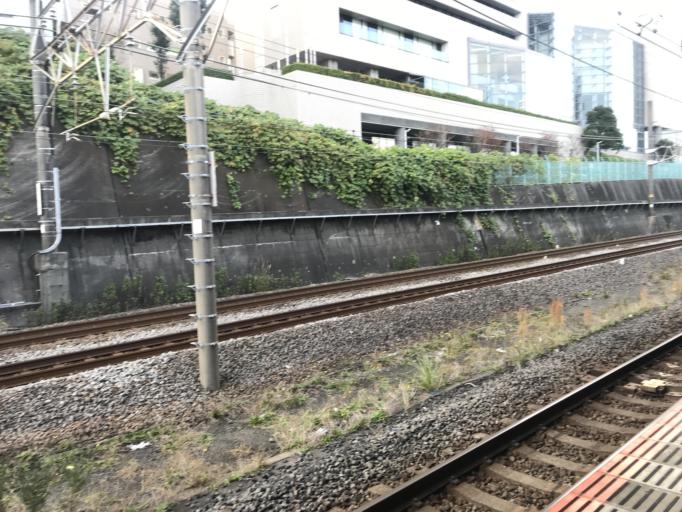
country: JP
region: Kanagawa
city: Yokohama
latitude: 35.4312
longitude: 139.5567
